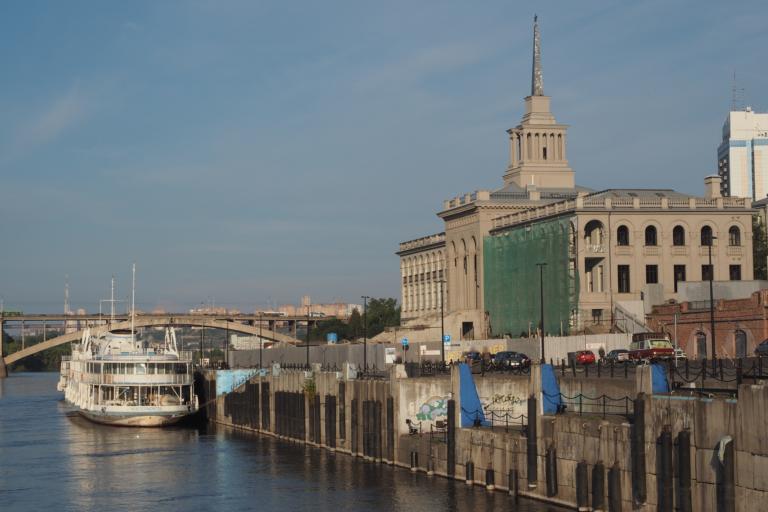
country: RU
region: Krasnoyarskiy
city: Krasnoyarsk
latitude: 56.0081
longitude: 92.8854
